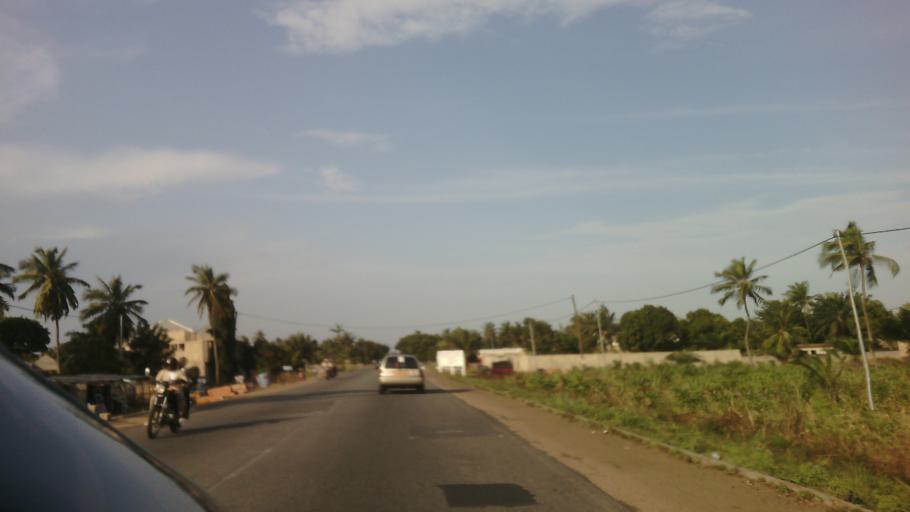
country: TG
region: Maritime
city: Vogan
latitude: 6.1965
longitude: 1.4015
